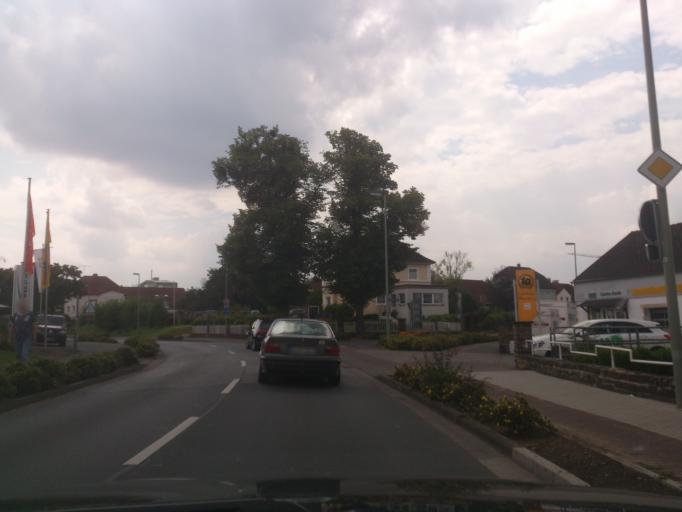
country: DE
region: North Rhine-Westphalia
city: Brakel
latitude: 51.7136
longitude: 9.1790
